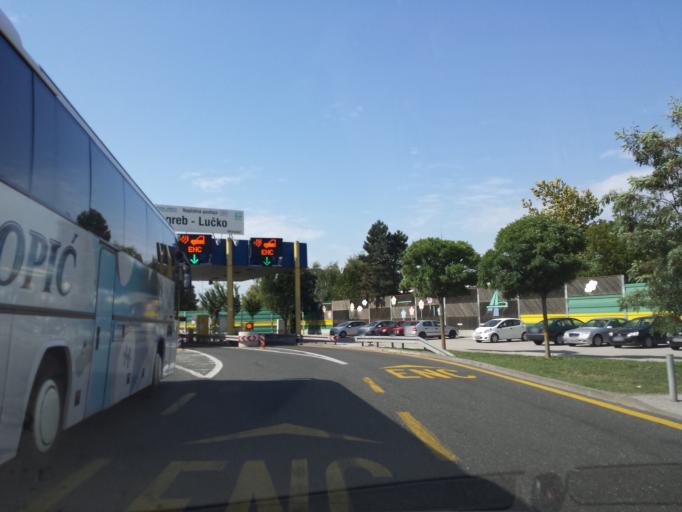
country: HR
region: Grad Zagreb
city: Brezovica
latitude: 45.7496
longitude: 15.8842
